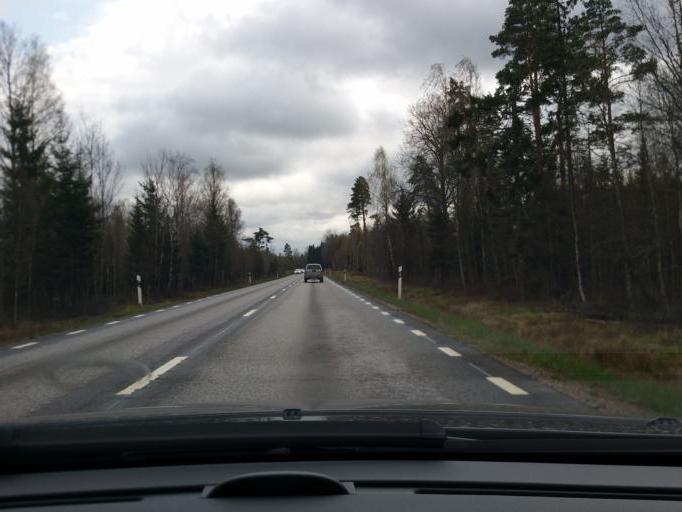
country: SE
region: Kronoberg
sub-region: Vaxjo Kommun
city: Ingelstad
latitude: 56.7897
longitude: 14.8971
